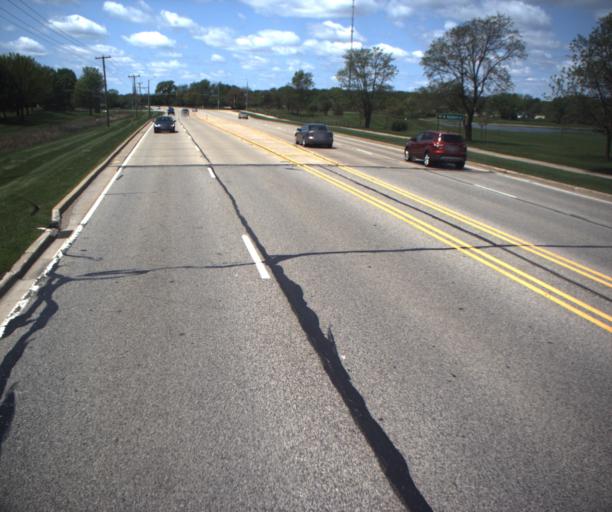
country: US
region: Illinois
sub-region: Kane County
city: Geneva
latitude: 41.8687
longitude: -88.2914
